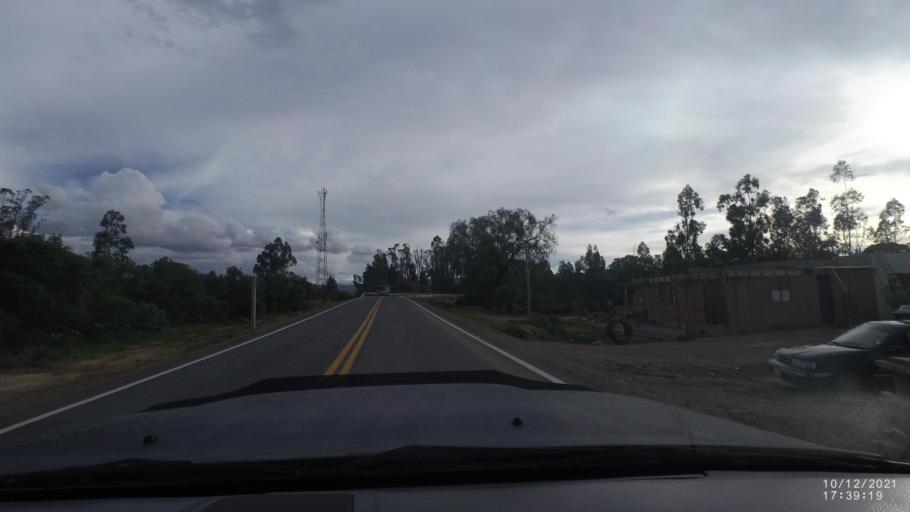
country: BO
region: Cochabamba
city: Tarata
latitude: -17.5780
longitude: -66.0140
